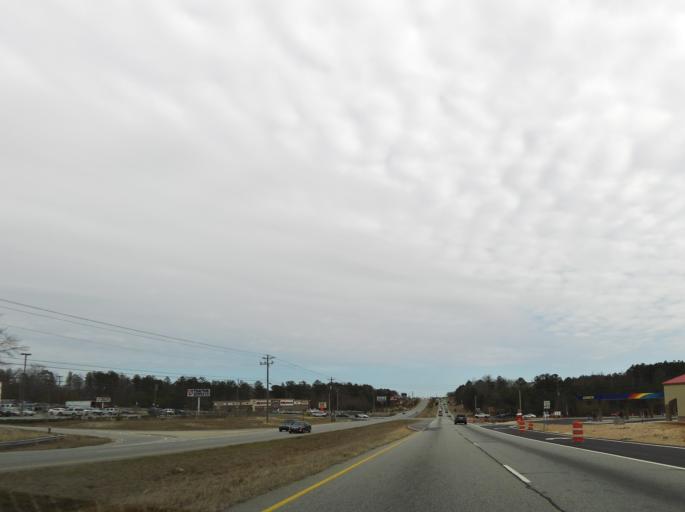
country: US
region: Georgia
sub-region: Houston County
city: Centerville
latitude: 32.6144
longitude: -83.7130
